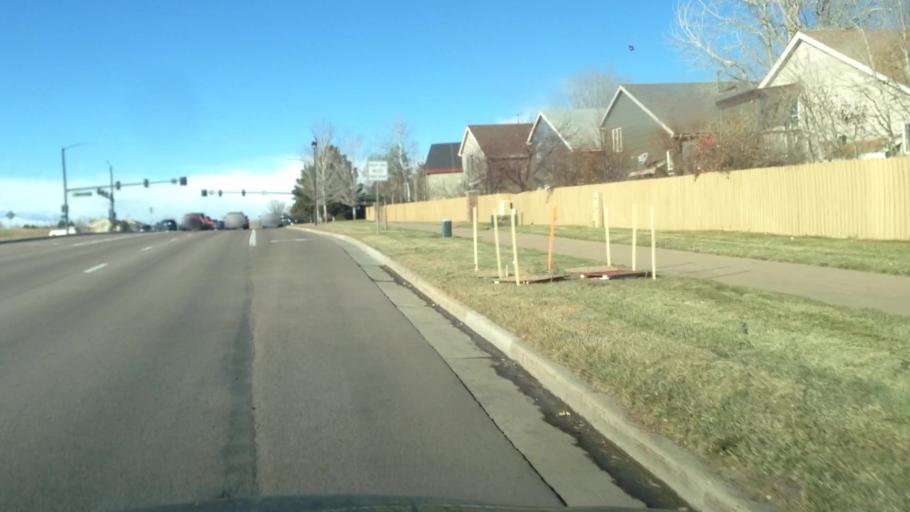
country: US
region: Colorado
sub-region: Douglas County
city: Stonegate
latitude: 39.5150
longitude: -104.7916
